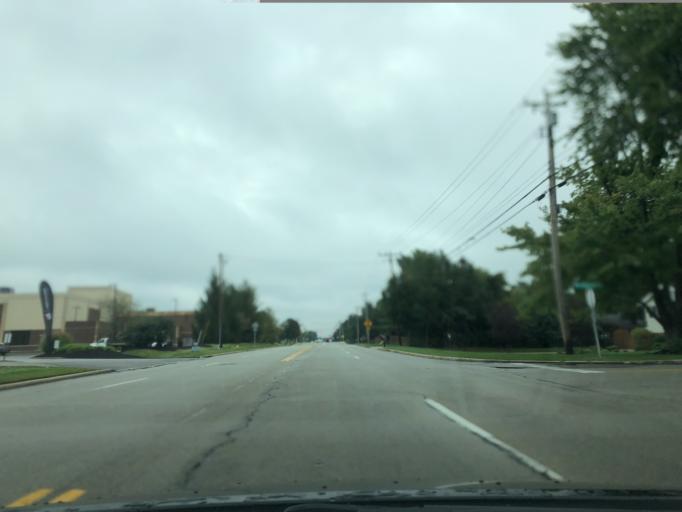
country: US
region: Ohio
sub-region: Hamilton County
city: Sixteen Mile Stand
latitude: 39.2771
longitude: -84.3392
